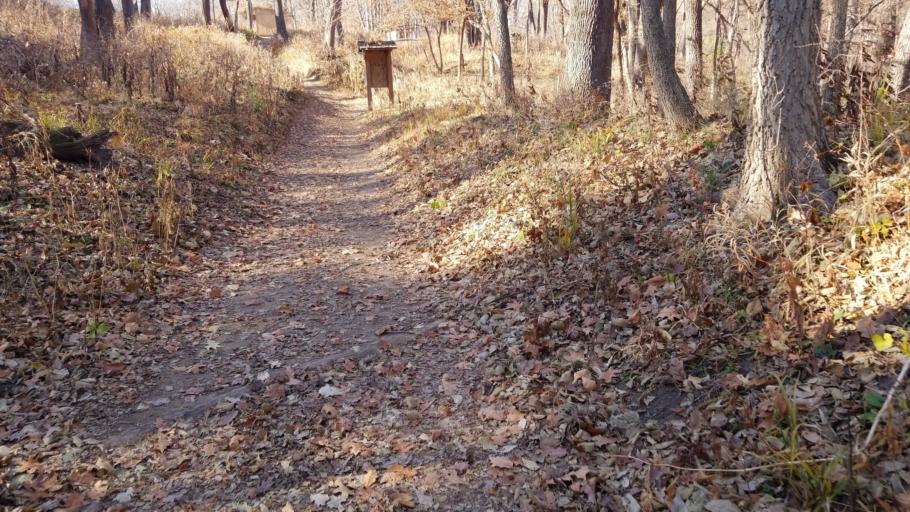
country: US
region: Nebraska
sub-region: Sarpy County
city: Bellevue
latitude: 41.1624
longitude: -95.8947
